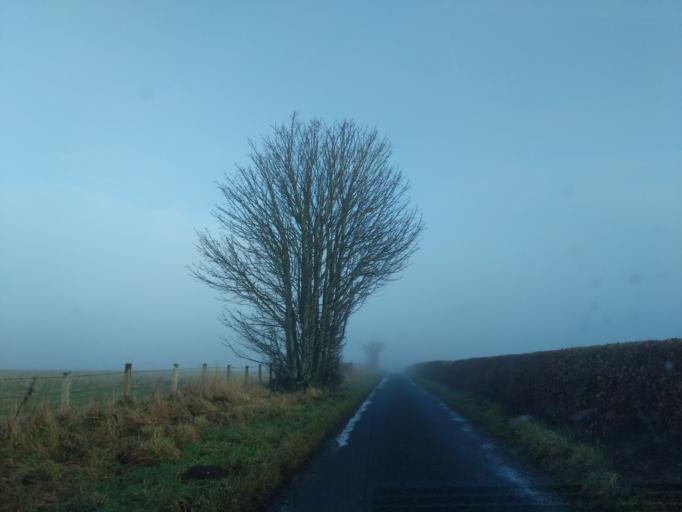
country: GB
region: Scotland
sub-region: Perth and Kinross
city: Auchterarder
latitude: 56.2840
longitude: -3.6906
